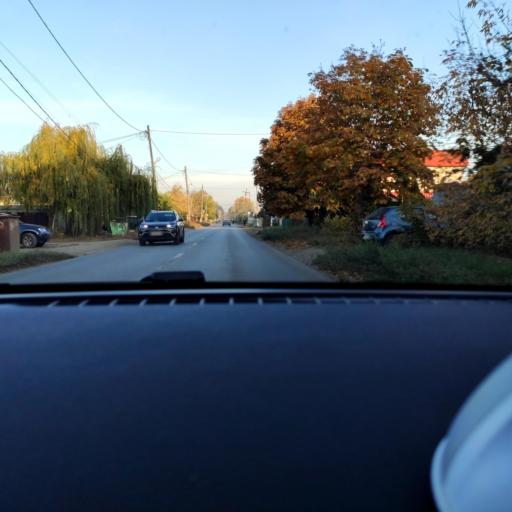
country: RU
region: Samara
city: Petra-Dubrava
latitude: 53.2550
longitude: 50.3128
